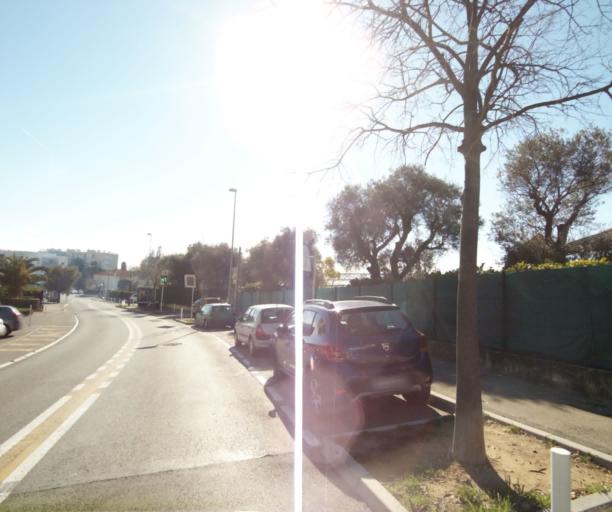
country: FR
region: Provence-Alpes-Cote d'Azur
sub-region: Departement des Alpes-Maritimes
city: Biot
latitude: 43.5960
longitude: 7.0990
